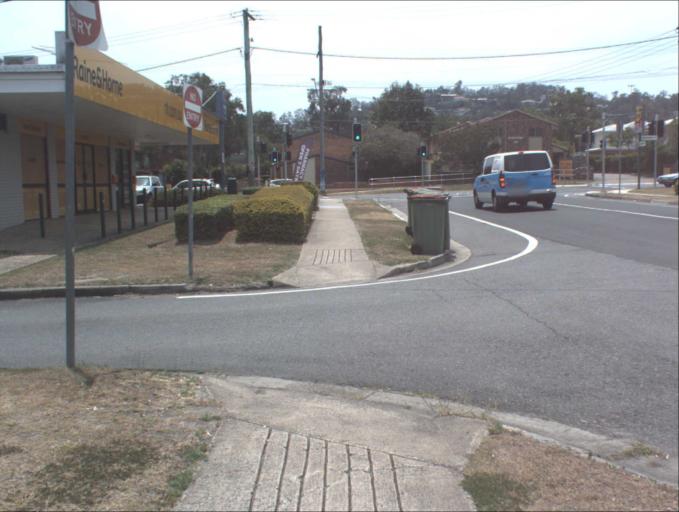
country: AU
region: Queensland
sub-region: Logan
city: Slacks Creek
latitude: -27.6660
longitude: 153.1856
